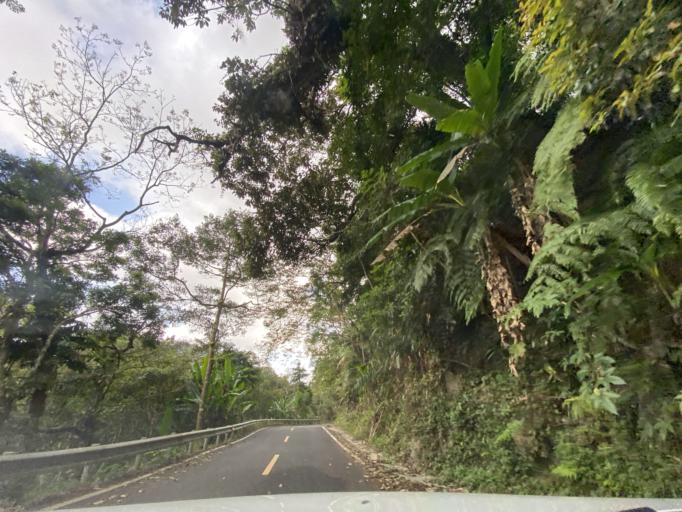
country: CN
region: Hainan
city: Diaoluoshan
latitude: 18.7064
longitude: 109.8822
